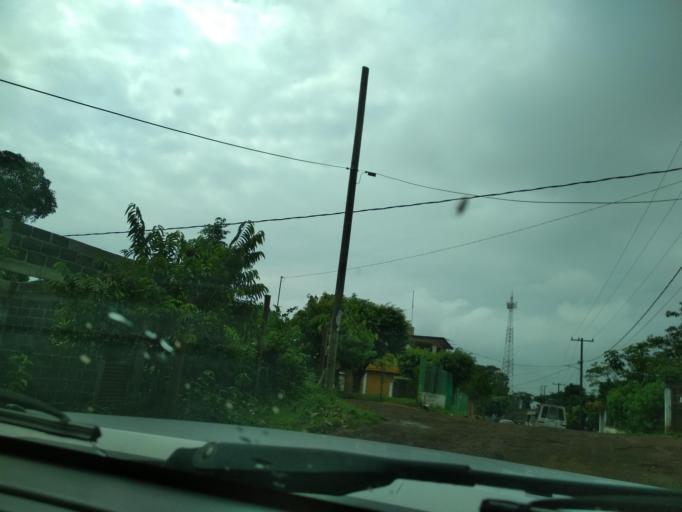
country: MX
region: Veracruz
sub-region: San Andres Tuxtla
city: Cerro las Iguanas
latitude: 18.4112
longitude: -95.1983
